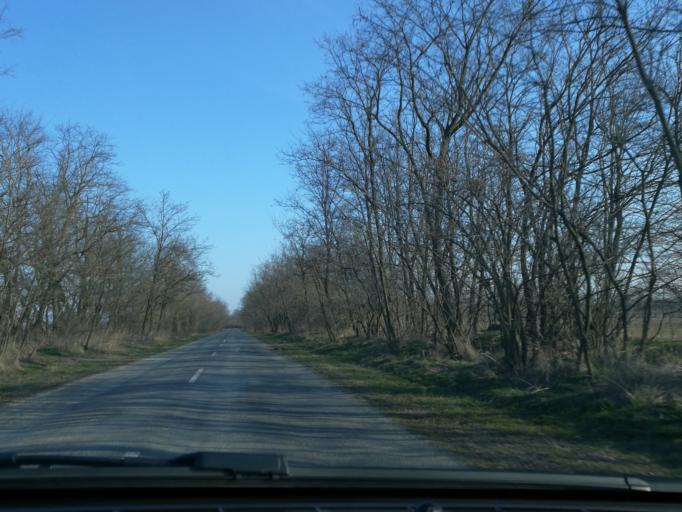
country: HU
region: Szabolcs-Szatmar-Bereg
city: Nyirbogdany
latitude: 48.0417
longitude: 21.9344
